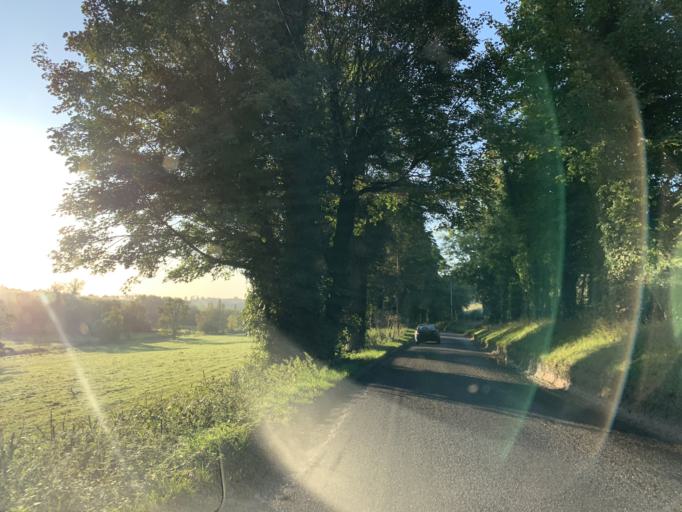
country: GB
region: England
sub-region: Wiltshire
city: Woodford
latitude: 51.1045
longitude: -1.8290
